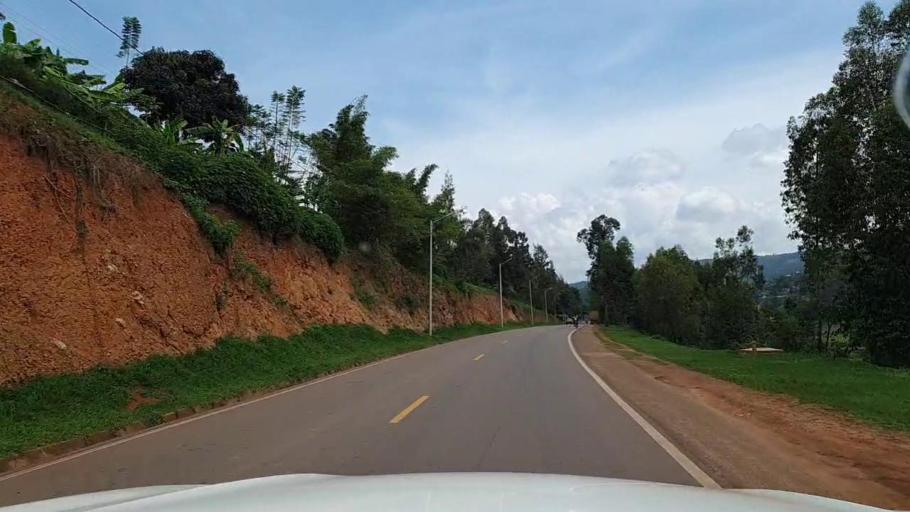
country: RW
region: Kigali
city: Kigali
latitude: -1.8719
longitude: 30.0832
